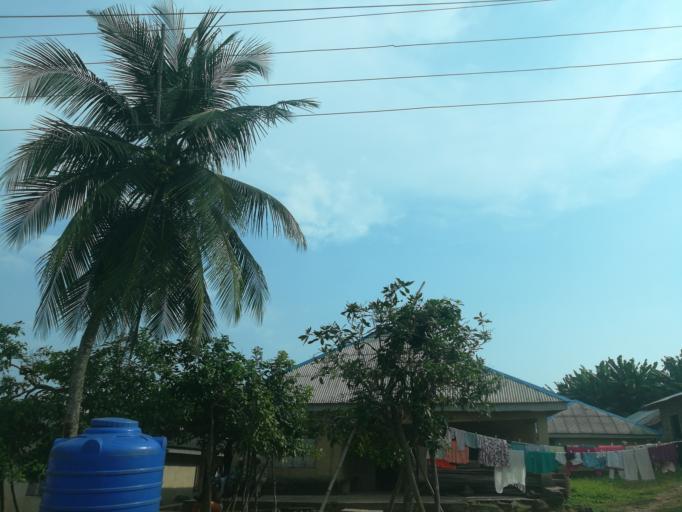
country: NG
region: Lagos
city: Ikorodu
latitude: 6.6626
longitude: 3.6720
